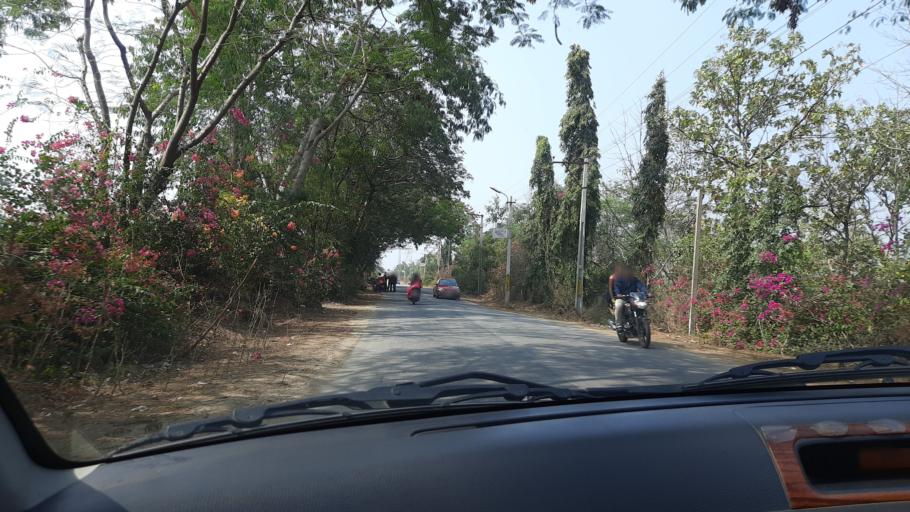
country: IN
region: Telangana
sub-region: Rangareddi
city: Lal Bahadur Nagar
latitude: 17.2795
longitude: 78.6530
